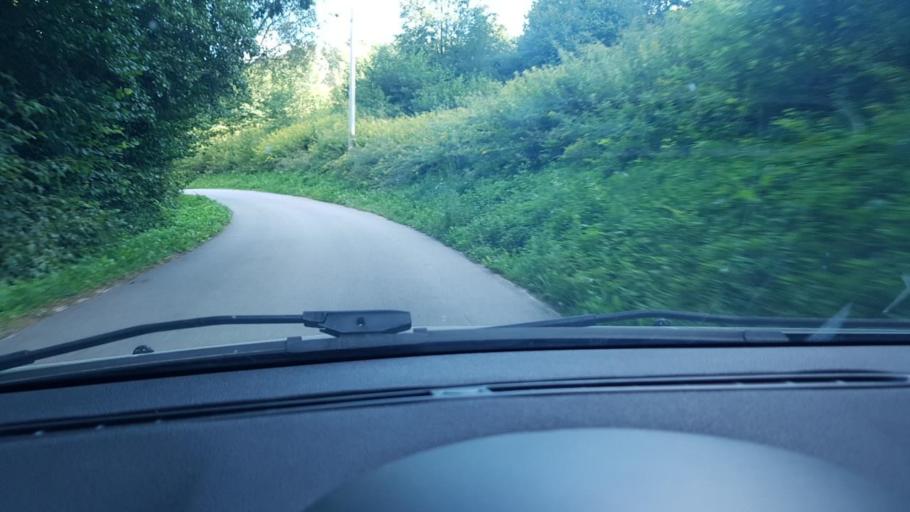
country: HR
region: Krapinsko-Zagorska
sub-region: Grad Krapina
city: Krapina
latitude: 46.1372
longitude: 15.8365
